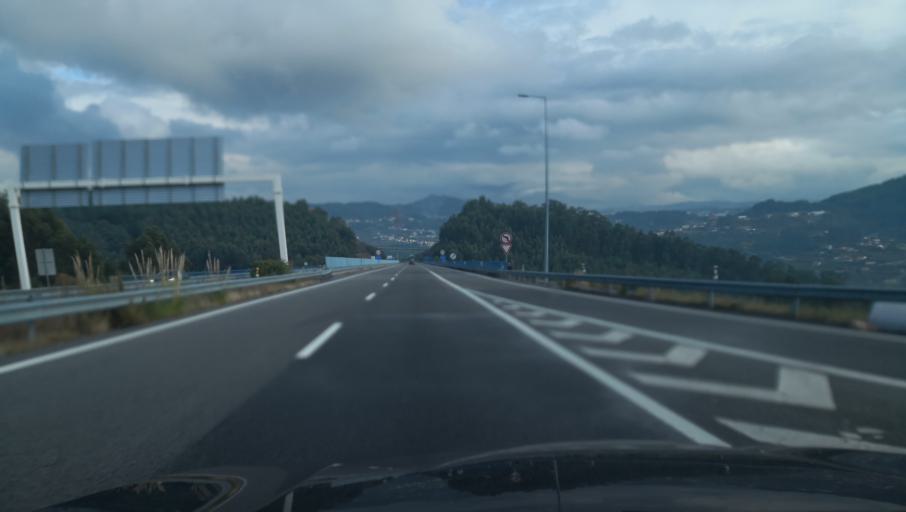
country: PT
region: Braga
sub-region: Vizela
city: Vizela
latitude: 41.4017
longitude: -8.2519
